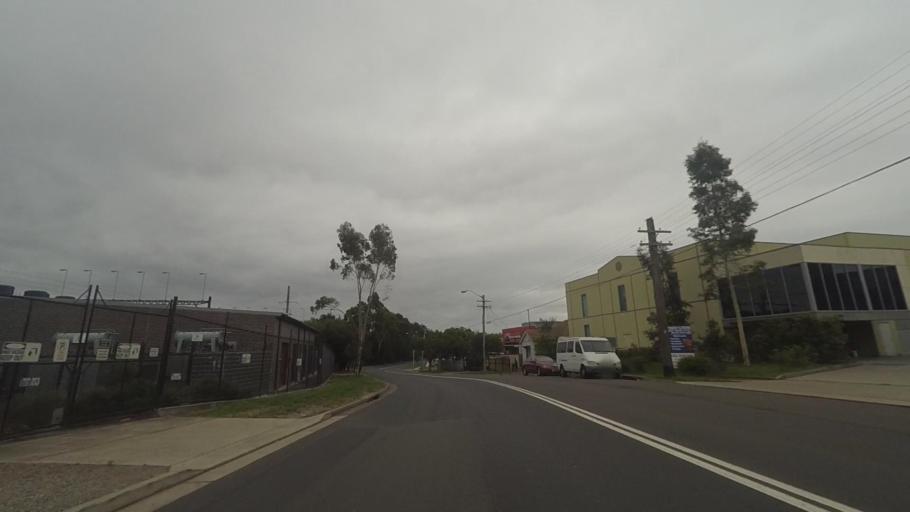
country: AU
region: New South Wales
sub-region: Auburn
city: Auburn
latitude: -33.8436
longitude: 151.0277
